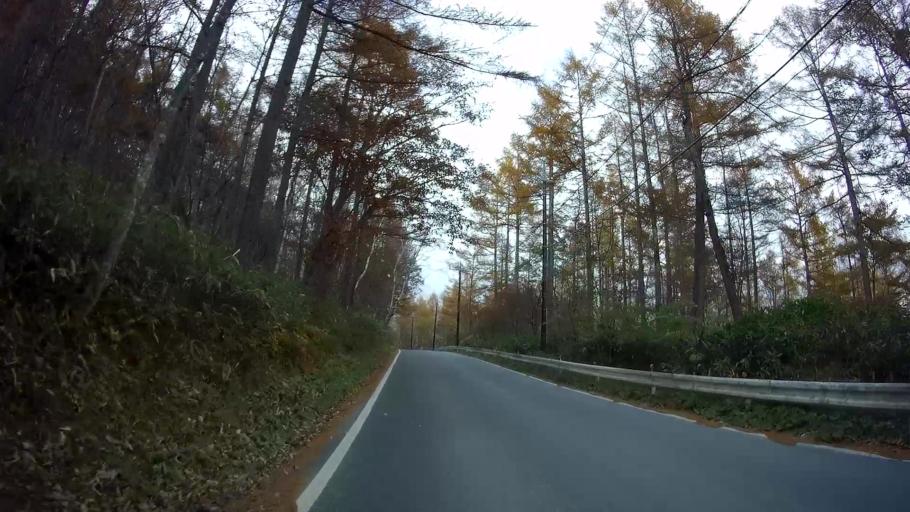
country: JP
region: Gunma
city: Nakanojomachi
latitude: 36.6706
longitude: 138.6714
